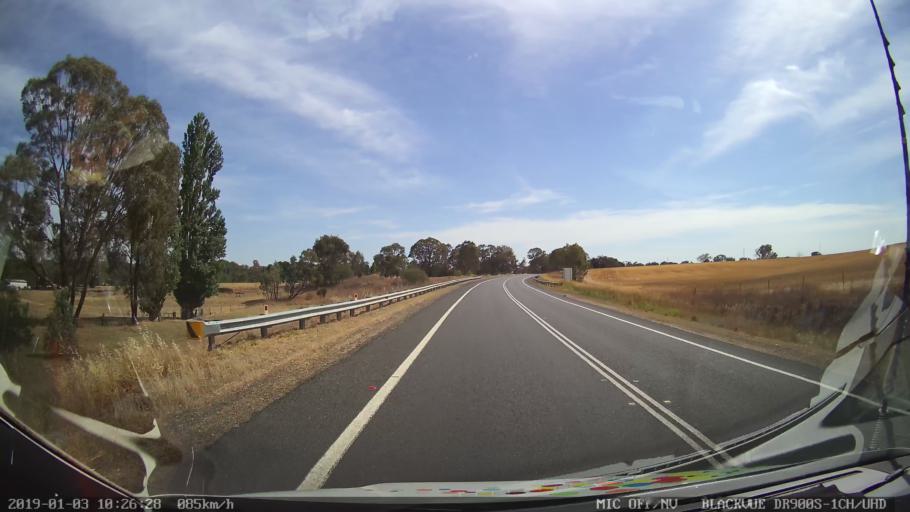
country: AU
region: New South Wales
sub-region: Young
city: Young
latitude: -34.4121
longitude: 148.2495
